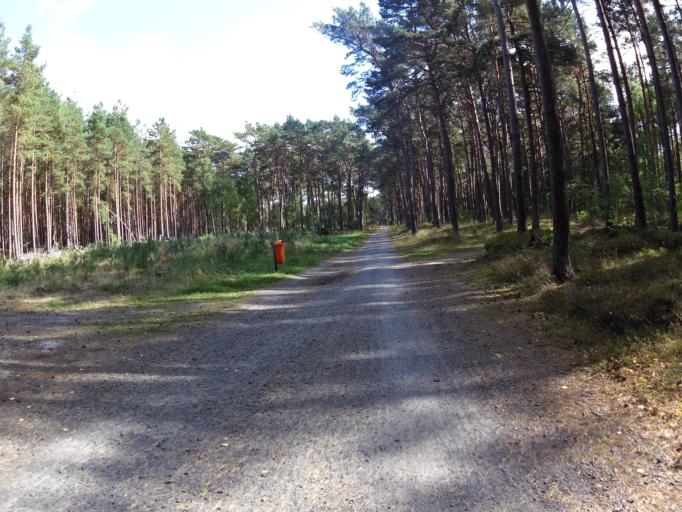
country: DE
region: Mecklenburg-Vorpommern
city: Karlshagen
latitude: 54.0946
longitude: 13.8707
